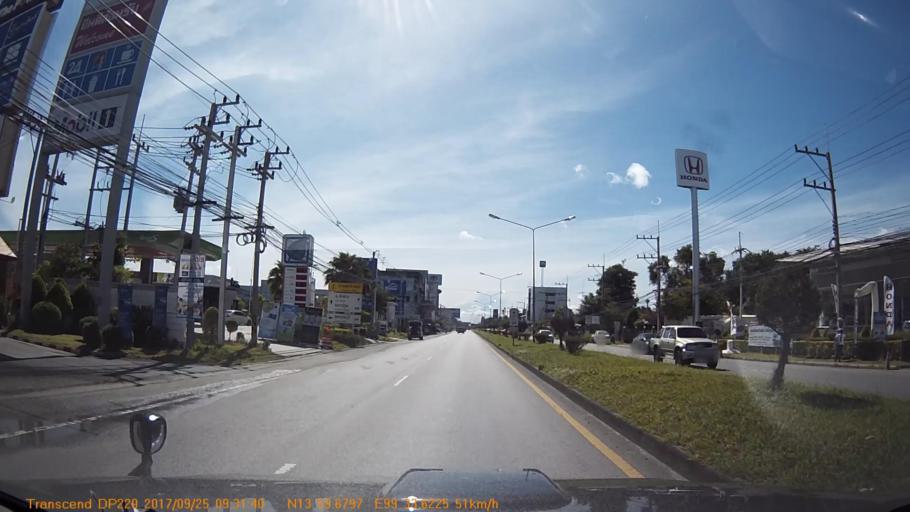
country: TH
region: Kanchanaburi
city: Kanchanaburi
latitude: 13.9946
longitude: 99.5605
